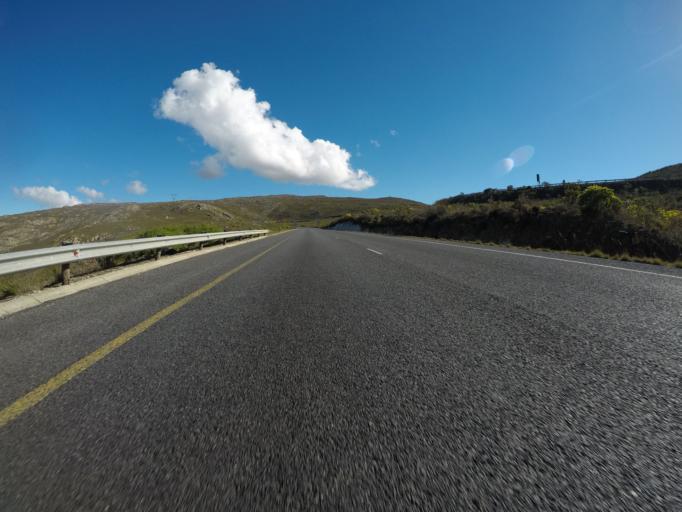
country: ZA
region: Western Cape
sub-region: Overberg District Municipality
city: Grabouw
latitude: -34.2221
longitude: 19.1782
